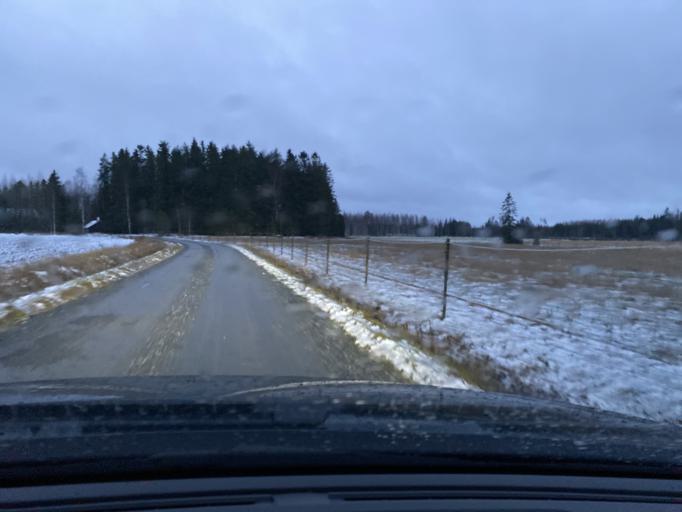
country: FI
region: Pirkanmaa
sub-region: Lounais-Pirkanmaa
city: Punkalaidun
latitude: 61.1181
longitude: 23.0224
